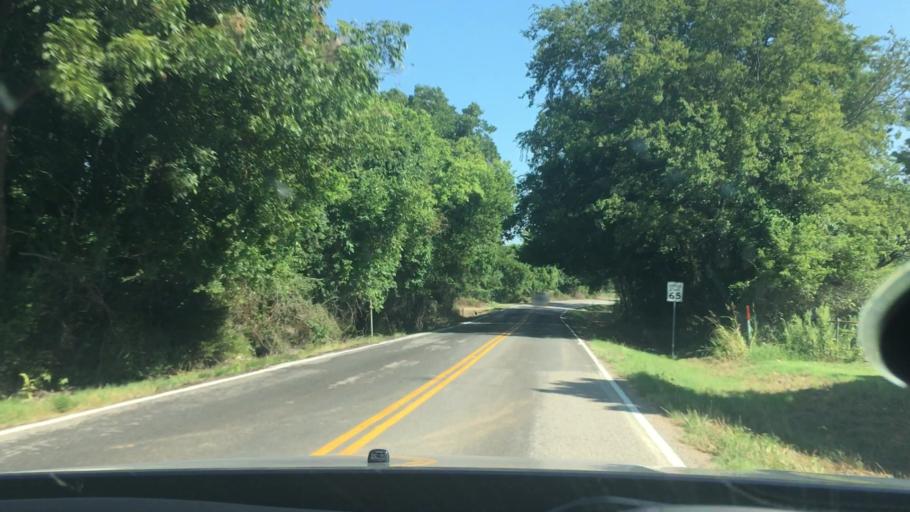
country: US
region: Oklahoma
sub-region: Johnston County
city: Tishomingo
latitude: 34.2076
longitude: -96.5428
